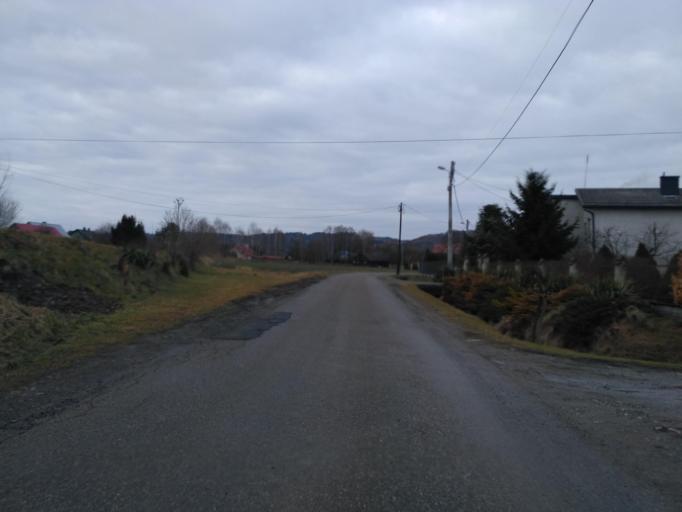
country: PL
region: Subcarpathian Voivodeship
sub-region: Powiat przemyski
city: Przedmiescie Dubieckie
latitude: 49.8294
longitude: 22.3794
